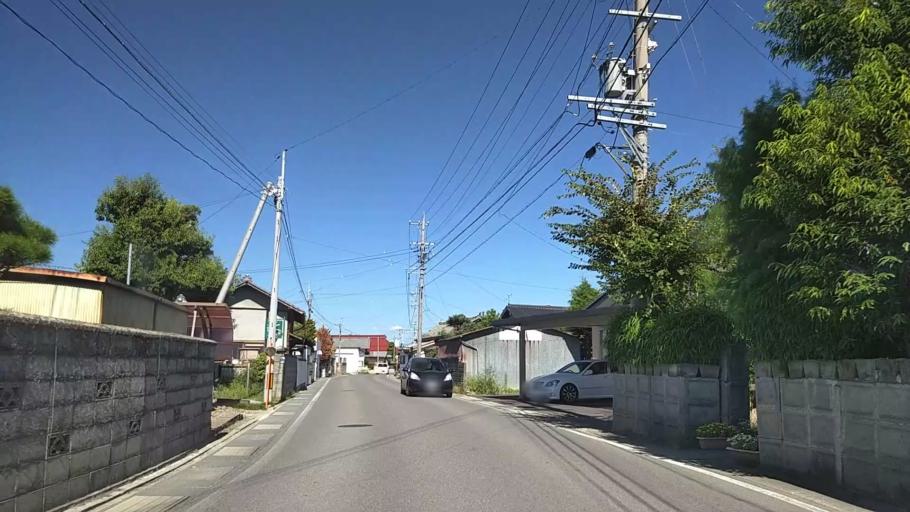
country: JP
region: Nagano
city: Nagano-shi
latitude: 36.6115
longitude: 138.1631
